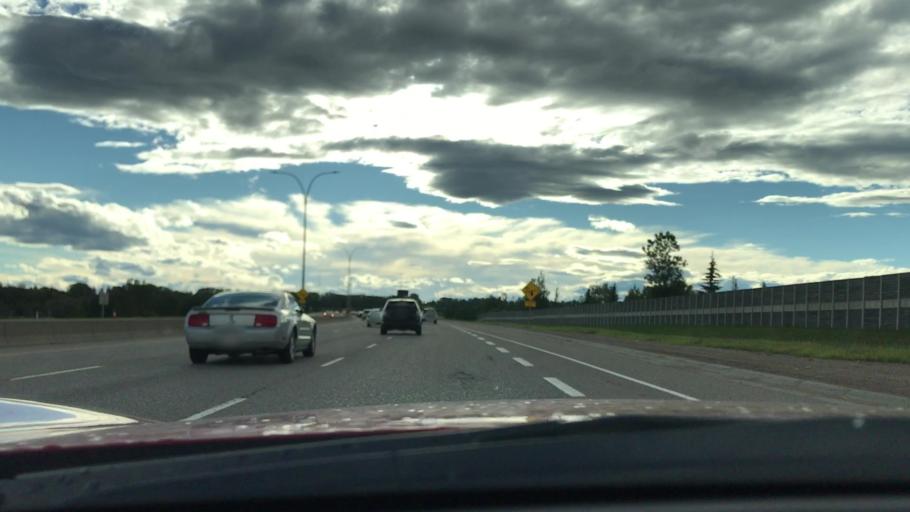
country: CA
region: Alberta
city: Calgary
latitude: 50.9517
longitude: -114.0145
